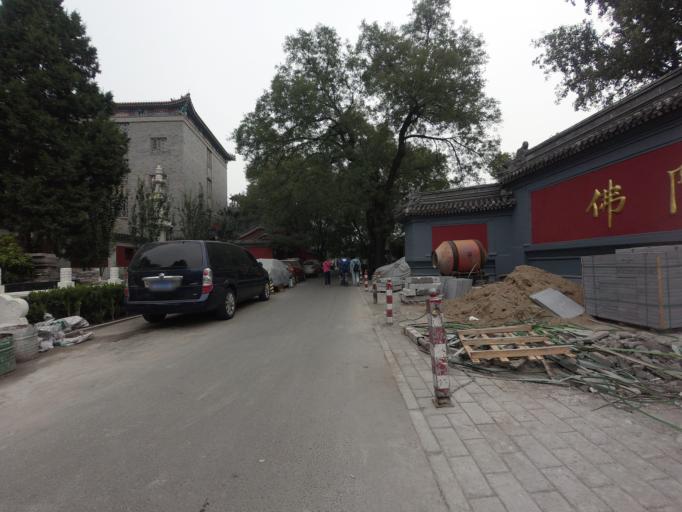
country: CN
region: Beijing
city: Jingshan
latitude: 39.9395
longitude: 116.3843
